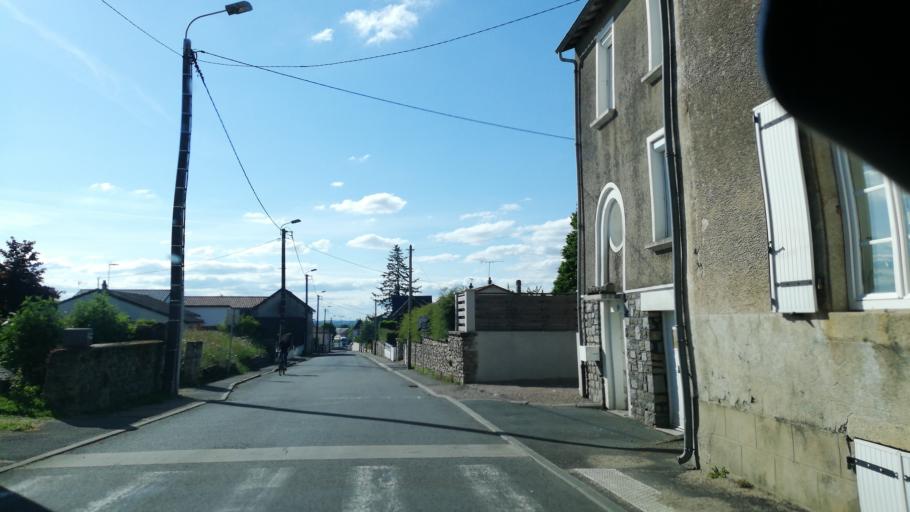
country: FR
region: Poitou-Charentes
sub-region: Departement des Deux-Sevres
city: Moncoutant
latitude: 46.7193
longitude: -0.5871
